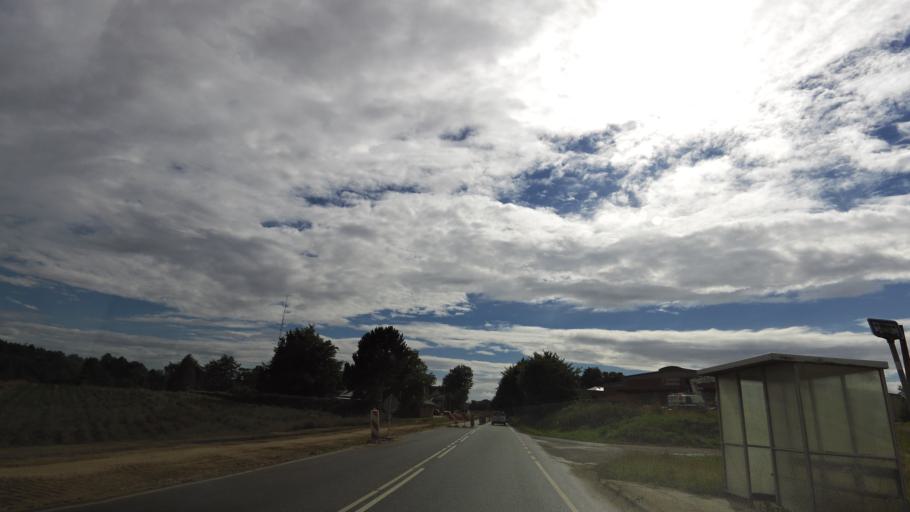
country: DK
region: South Denmark
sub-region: Nordfyns Kommune
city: Sonderso
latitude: 55.4630
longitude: 10.1960
